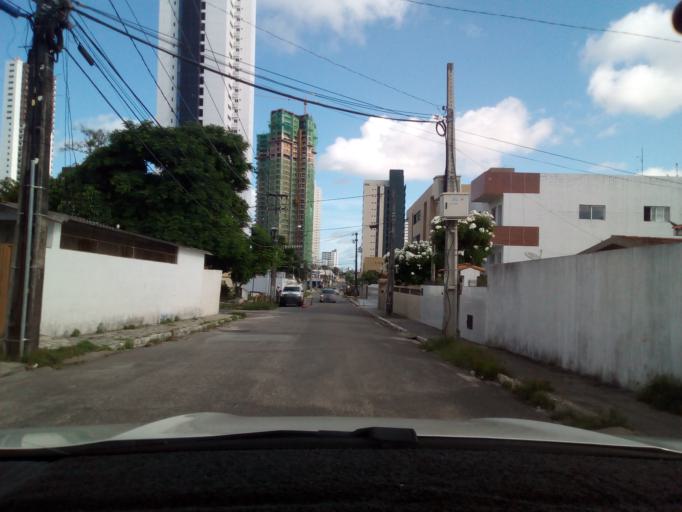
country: BR
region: Paraiba
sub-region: Joao Pessoa
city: Joao Pessoa
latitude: -7.1112
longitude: -34.8420
